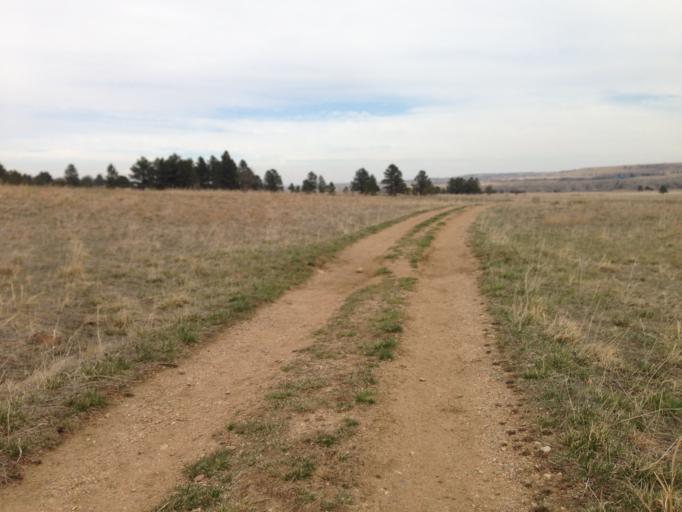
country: US
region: Colorado
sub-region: Boulder County
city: Boulder
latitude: 39.9556
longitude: -105.2578
